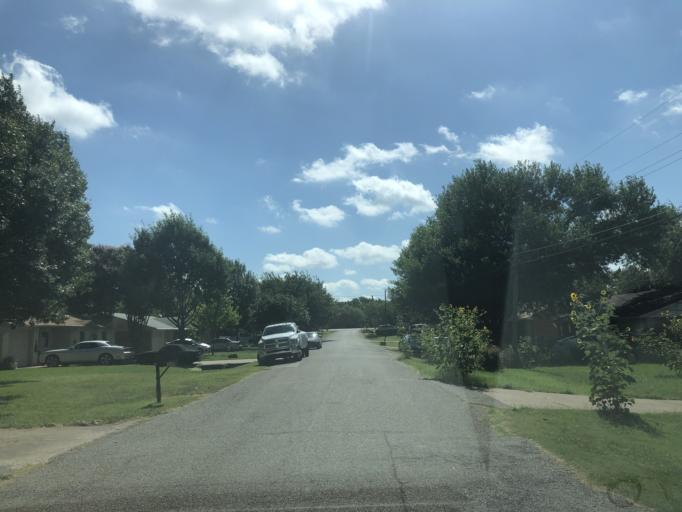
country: US
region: Texas
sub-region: Dallas County
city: Duncanville
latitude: 32.6581
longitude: -96.9192
